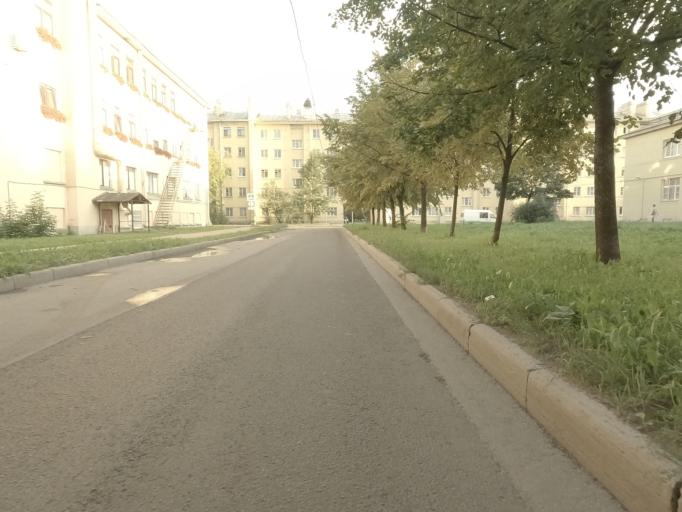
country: RU
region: St.-Petersburg
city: Admiralteisky
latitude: 59.8947
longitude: 30.2722
